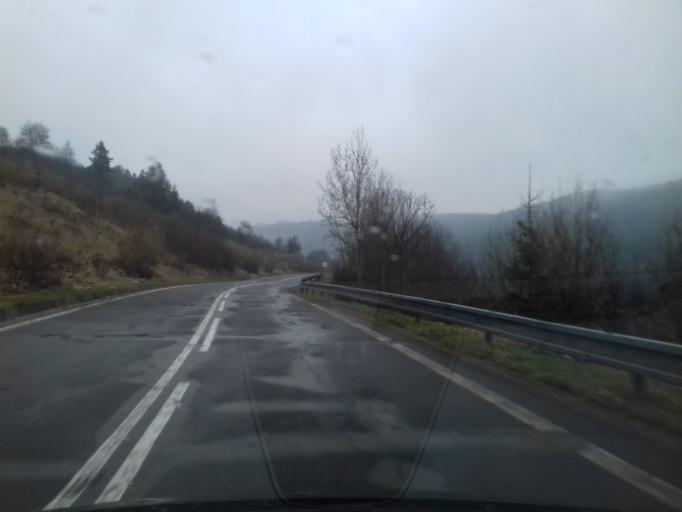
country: SK
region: Presovsky
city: Stara L'ubovna
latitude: 49.3582
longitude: 20.6972
